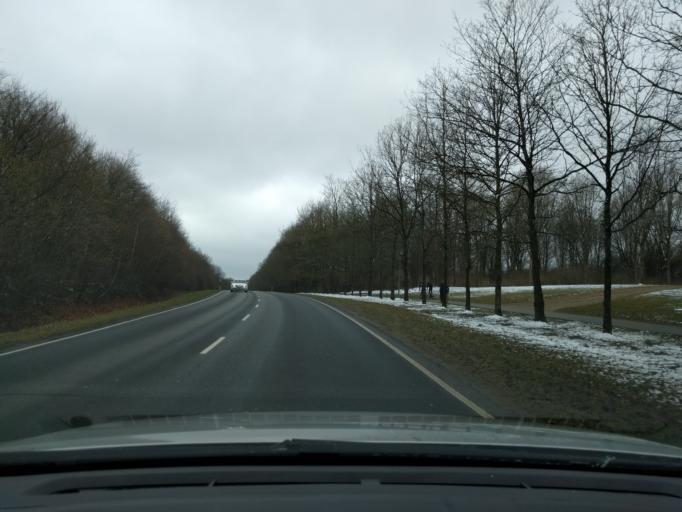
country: DK
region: South Denmark
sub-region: Odense Kommune
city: Odense
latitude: 55.3816
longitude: 10.3460
